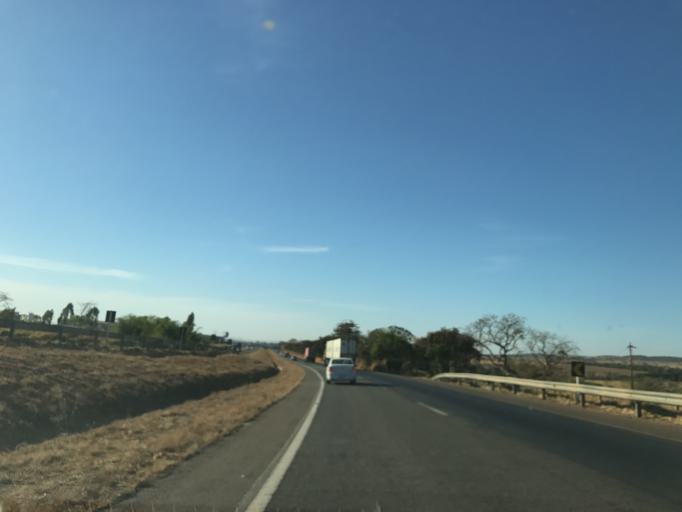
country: BR
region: Goias
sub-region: Hidrolandia
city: Hidrolandia
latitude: -16.9434
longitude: -49.2530
